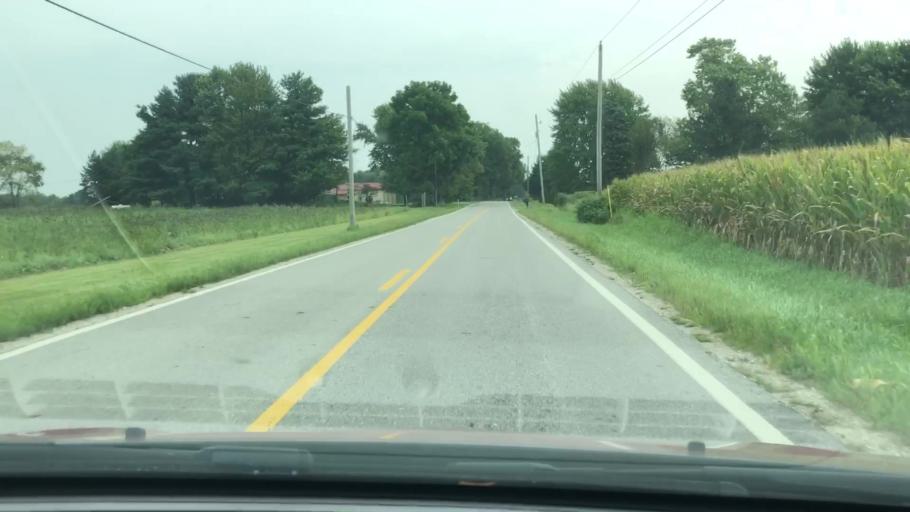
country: US
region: Ohio
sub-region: Delaware County
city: Sunbury
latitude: 40.2164
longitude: -82.8199
